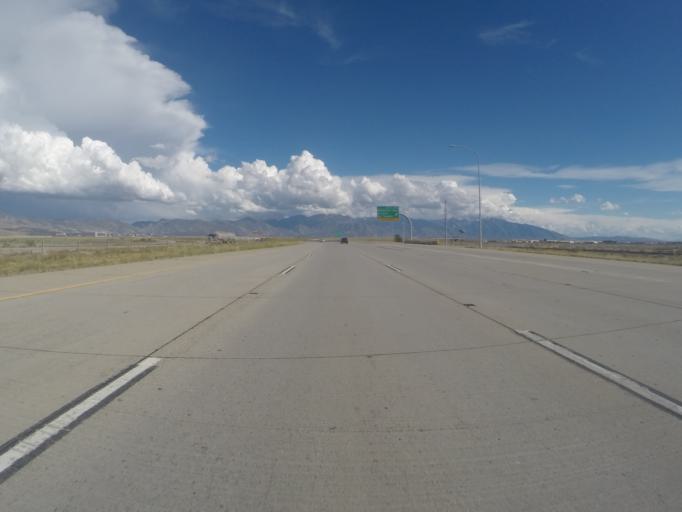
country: US
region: Utah
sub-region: Salt Lake County
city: West Valley City
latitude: 40.7669
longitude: -111.9973
